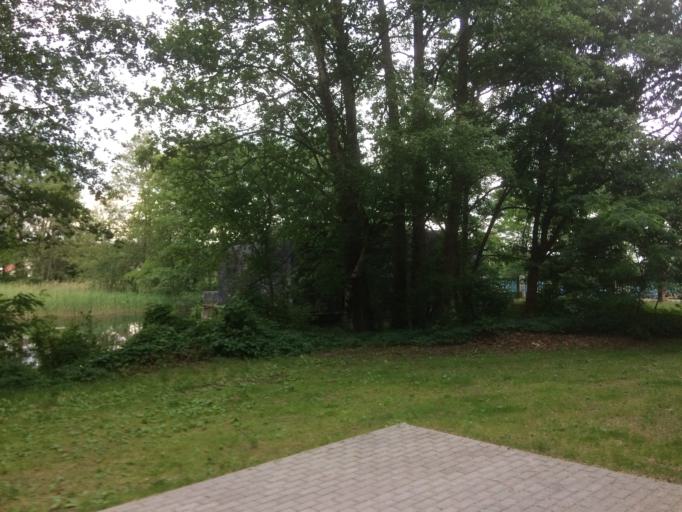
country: PL
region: Lubusz
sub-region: Powiat swiebodzinski
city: Skape
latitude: 52.2099
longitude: 15.4256
